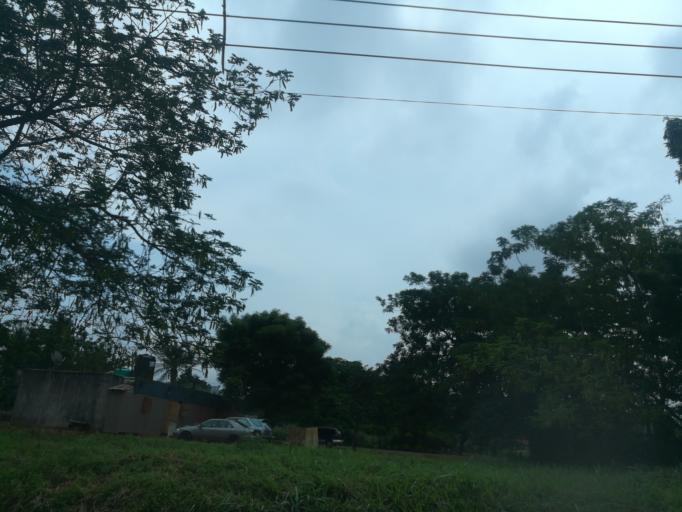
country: NG
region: Lagos
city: Oshodi
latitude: 6.5657
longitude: 3.3610
